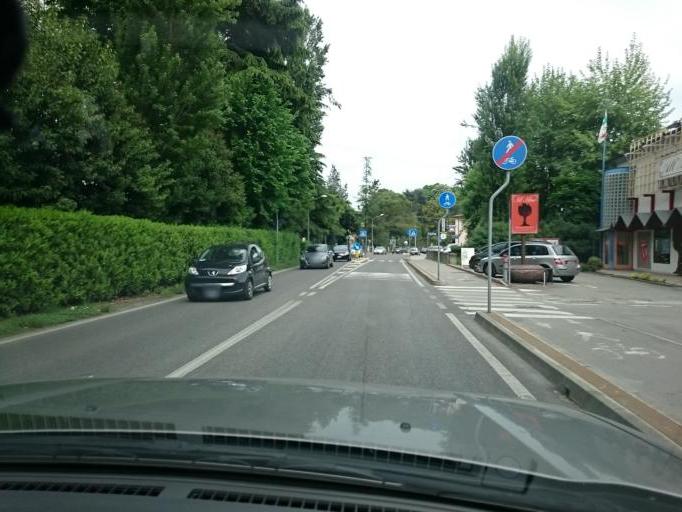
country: IT
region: Veneto
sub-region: Provincia di Padova
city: San Vito
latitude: 45.4142
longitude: 11.9664
